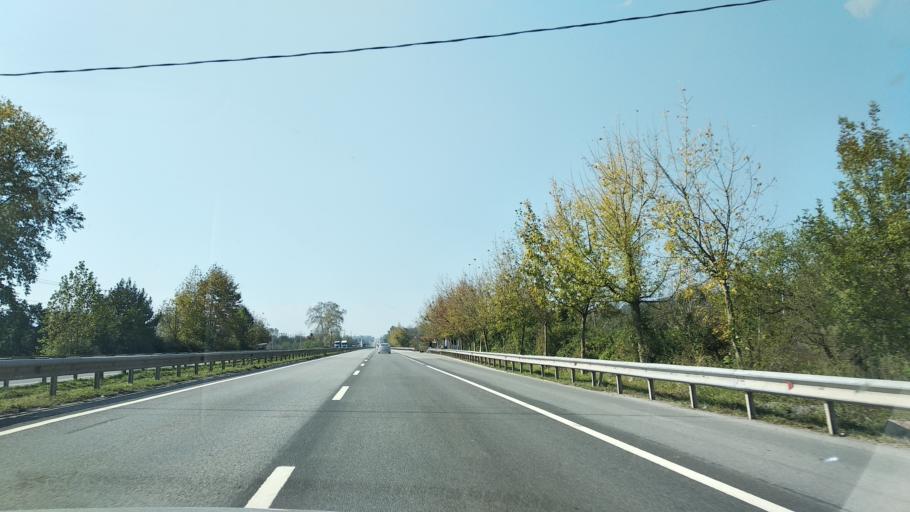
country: TR
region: Sakarya
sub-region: Merkez
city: Sapanca
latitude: 40.7327
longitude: 30.2033
